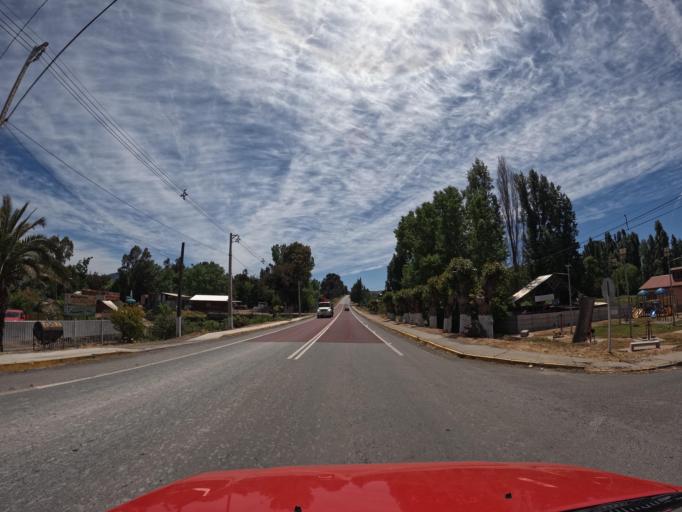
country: CL
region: Maule
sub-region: Provincia de Talca
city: Talca
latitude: -35.3024
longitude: -71.5226
